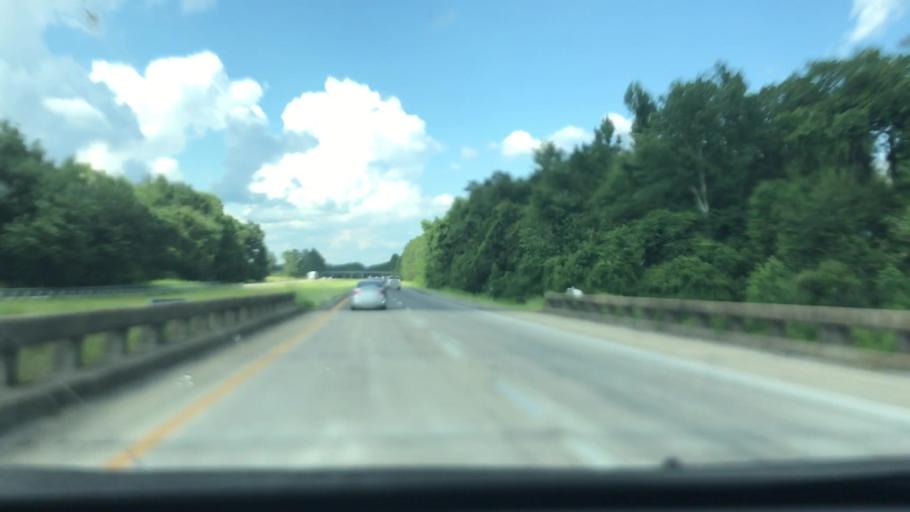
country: US
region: South Carolina
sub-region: Clarendon County
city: Manning
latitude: 33.8127
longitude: -80.1514
